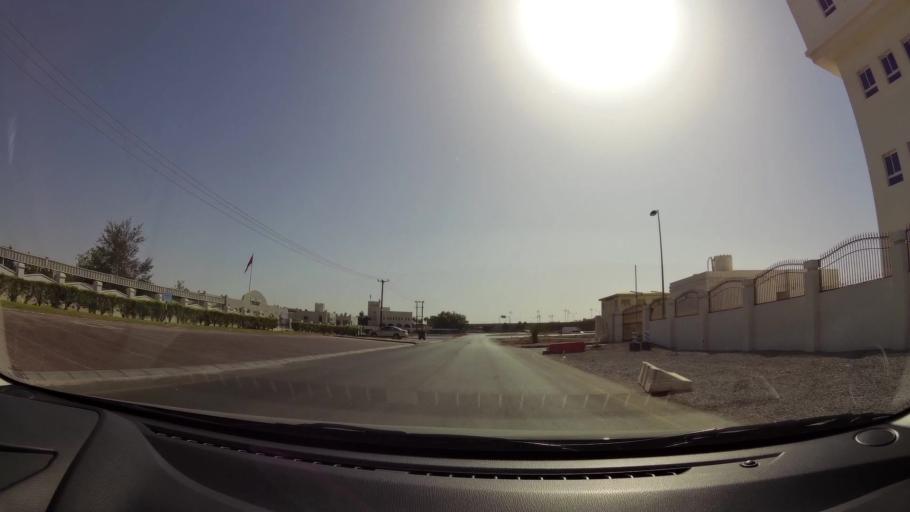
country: OM
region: Muhafazat Masqat
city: Bawshar
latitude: 23.5842
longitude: 58.2987
